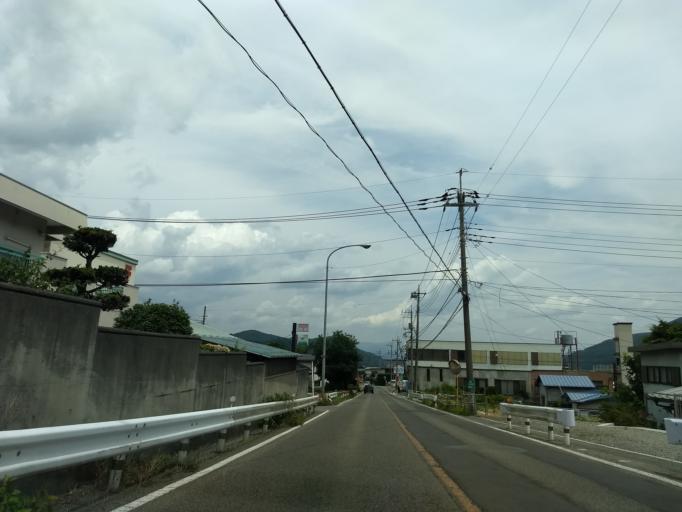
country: JP
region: Yamanashi
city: Otsuki
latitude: 35.5107
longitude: 138.8291
